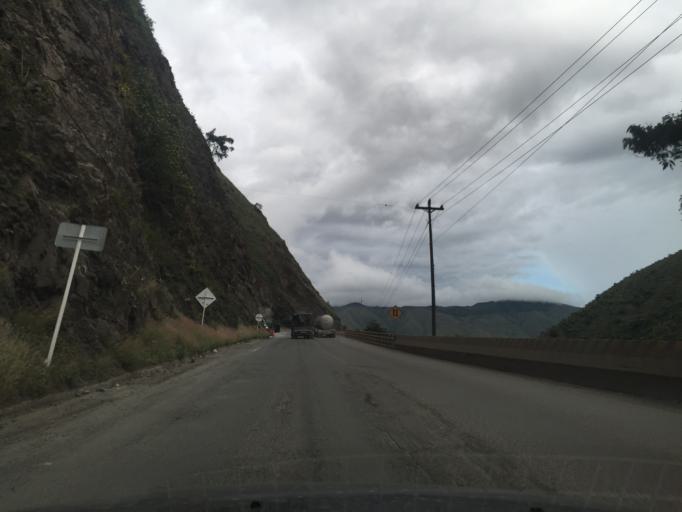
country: CO
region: Valle del Cauca
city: Dagua
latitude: 3.7713
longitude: -76.6840
